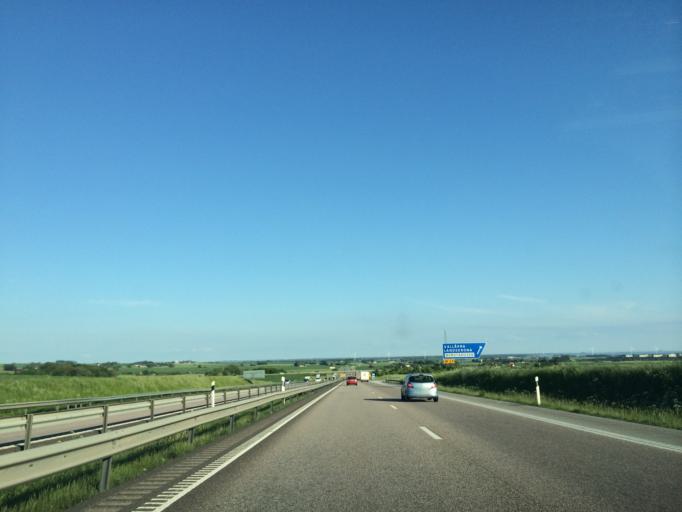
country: SE
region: Skane
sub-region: Helsingborg
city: Glumslov
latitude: 55.9282
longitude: 12.8303
